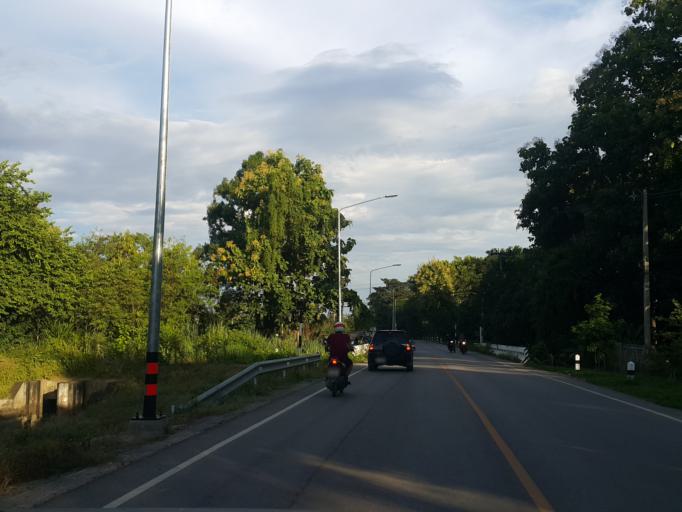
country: TH
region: Chiang Mai
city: San Sai
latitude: 18.9035
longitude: 99.0168
